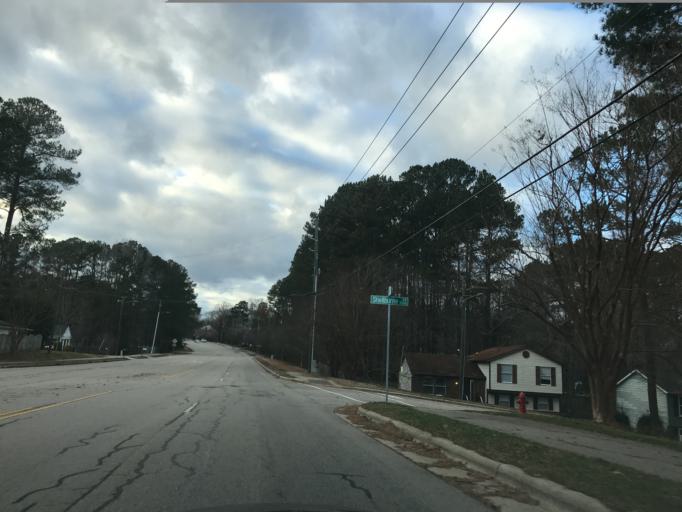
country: US
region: North Carolina
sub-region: Wake County
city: West Raleigh
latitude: 35.8709
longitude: -78.6555
